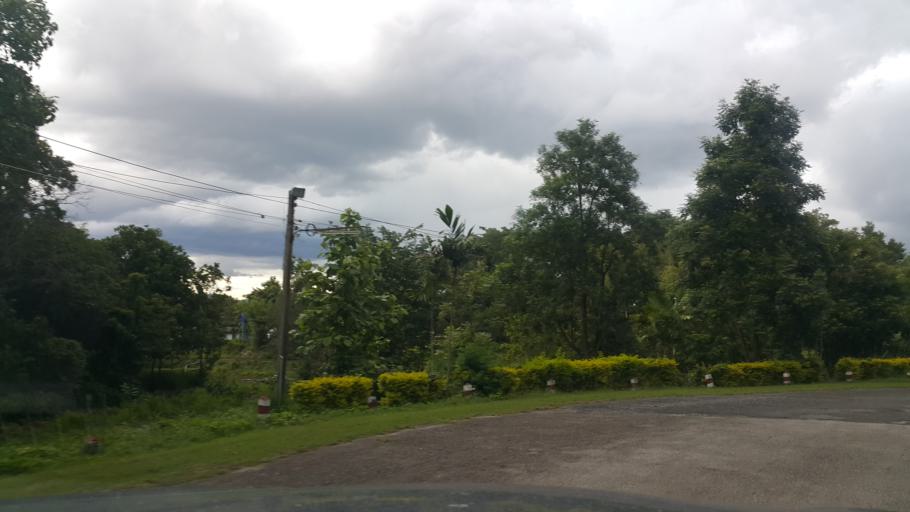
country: TH
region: Chiang Mai
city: Mae Taeng
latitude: 19.1832
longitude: 98.9674
